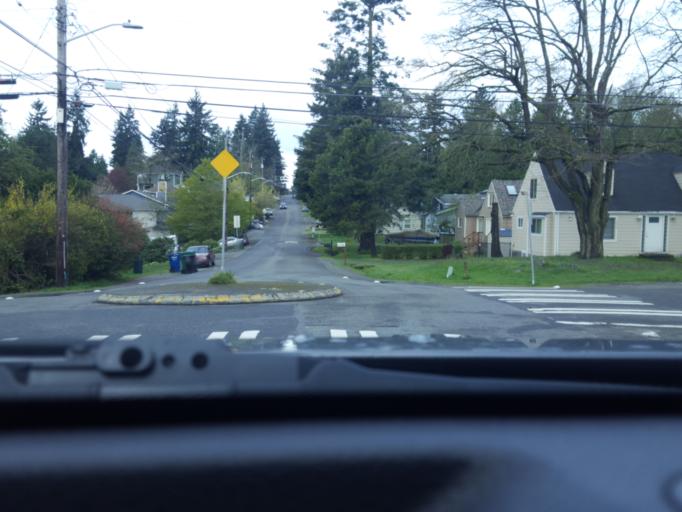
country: US
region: Washington
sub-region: King County
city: Shoreline
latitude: 47.7140
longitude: -122.3149
